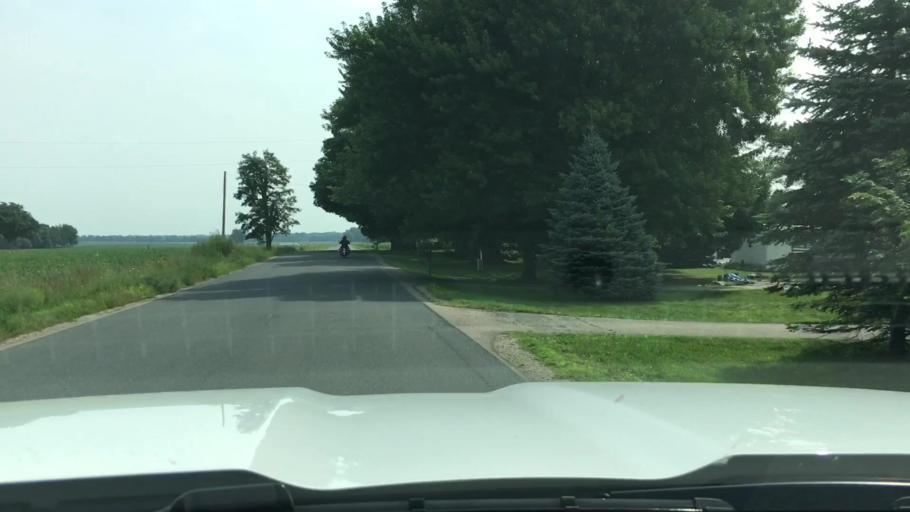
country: US
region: Michigan
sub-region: Eaton County
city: Grand Ledge
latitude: 42.7849
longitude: -84.7531
